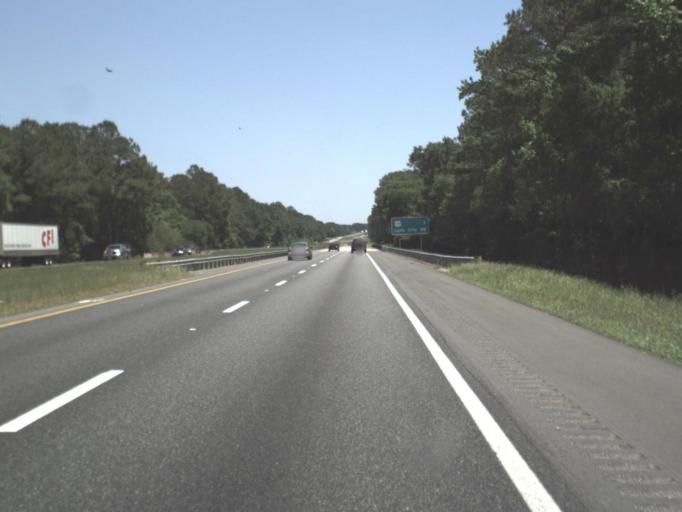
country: US
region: Florida
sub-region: Jefferson County
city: Monticello
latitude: 30.4893
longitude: -84.0075
